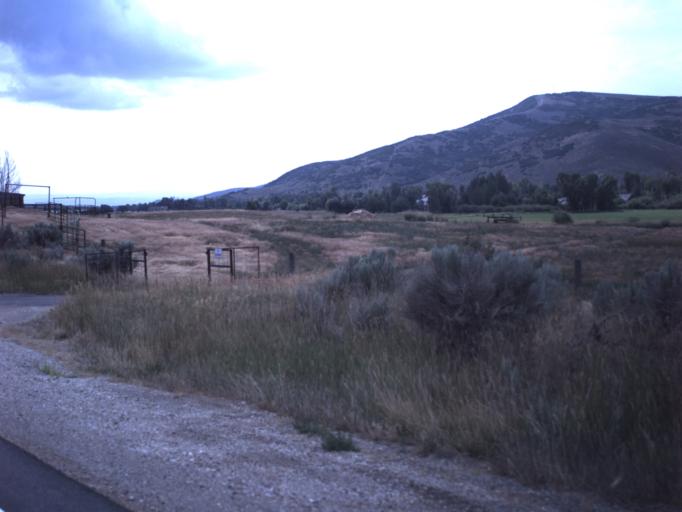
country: US
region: Utah
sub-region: Summit County
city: Oakley
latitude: 40.7481
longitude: -111.3634
